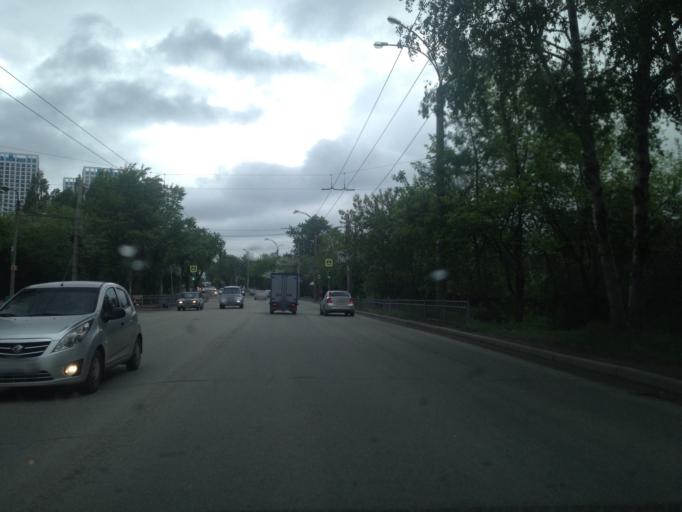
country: RU
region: Sverdlovsk
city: Yekaterinburg
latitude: 56.7730
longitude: 60.6678
